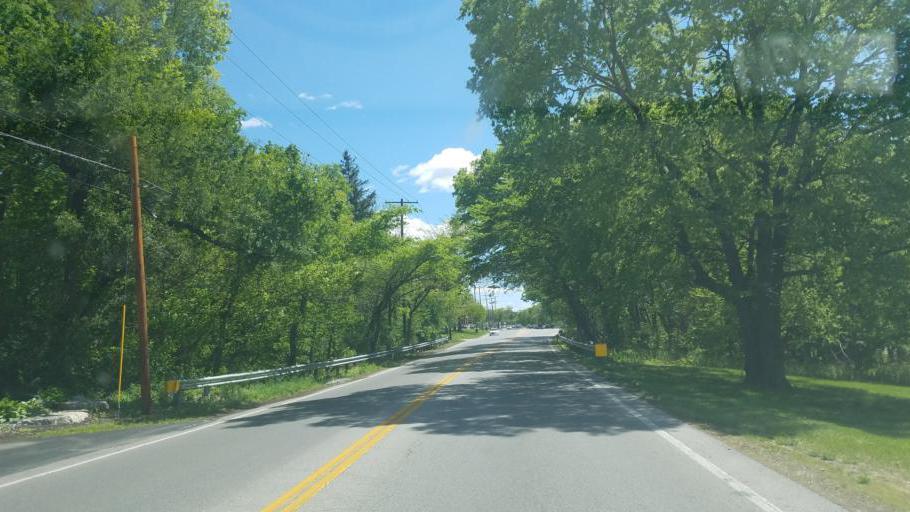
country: US
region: Ohio
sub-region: Franklin County
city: Upper Arlington
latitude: 40.0332
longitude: -83.0926
